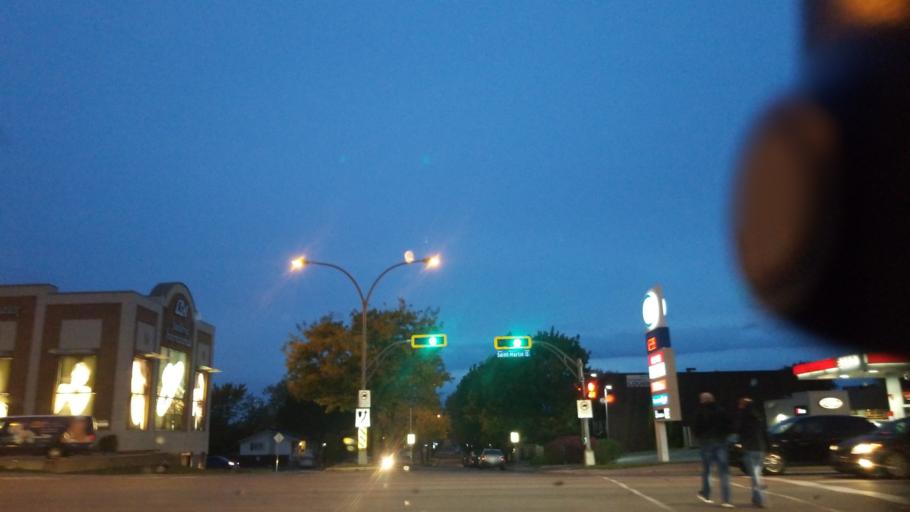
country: CA
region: Quebec
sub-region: Laval
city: Laval
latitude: 45.5706
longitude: -73.7228
